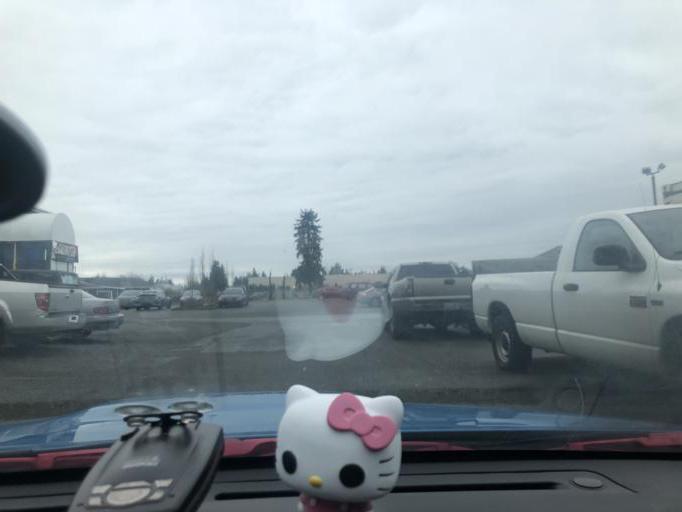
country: US
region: Washington
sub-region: Snohomish County
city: Smokey Point
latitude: 48.1489
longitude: -122.1817
